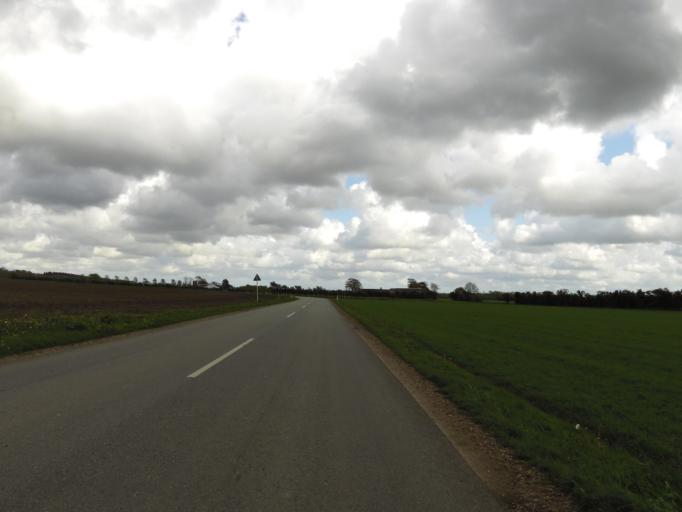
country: DK
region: South Denmark
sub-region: Haderslev Kommune
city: Gram
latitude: 55.3124
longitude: 8.9877
